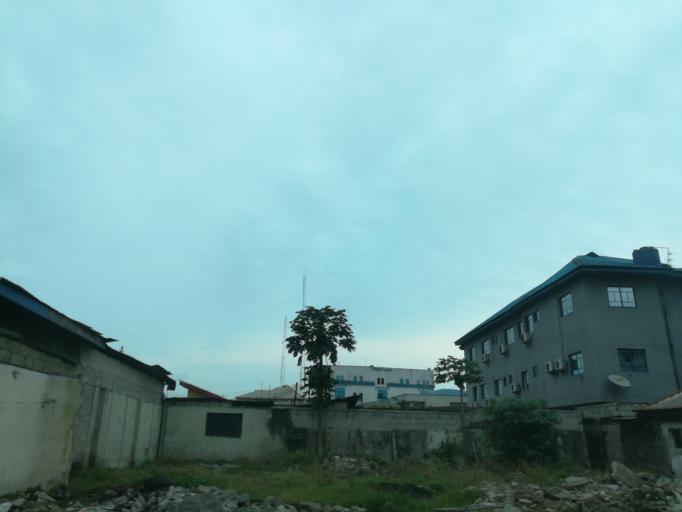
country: NG
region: Rivers
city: Port Harcourt
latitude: 4.8368
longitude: 7.0239
